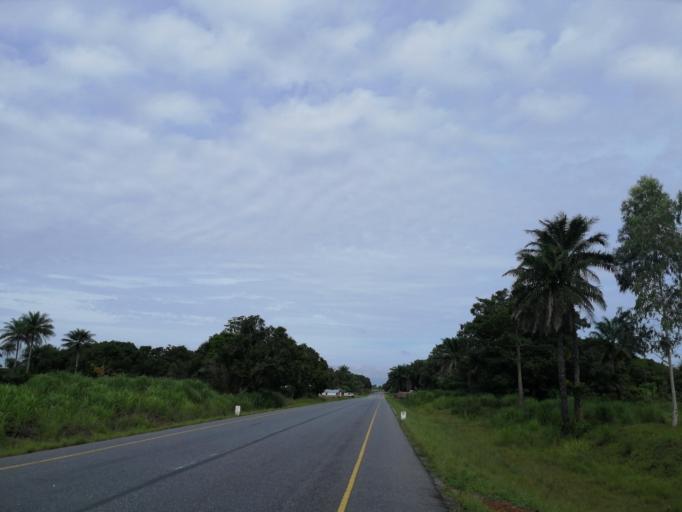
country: SL
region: Northern Province
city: Port Loko
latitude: 8.7726
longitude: -12.8671
